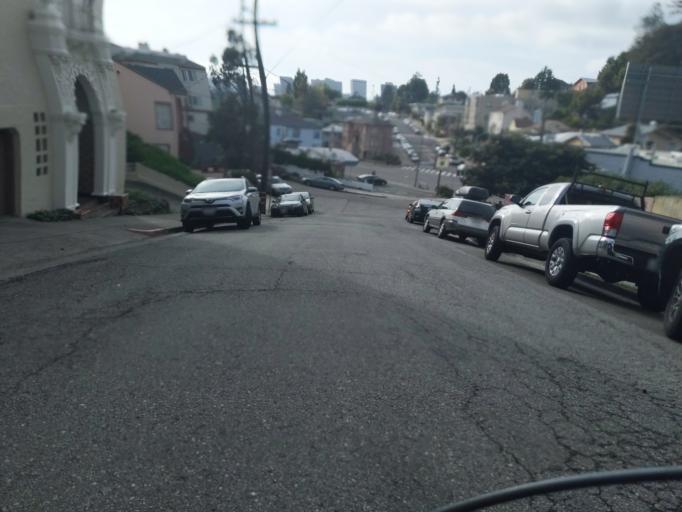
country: US
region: California
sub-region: Alameda County
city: Piedmont
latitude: 37.8018
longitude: -122.2410
